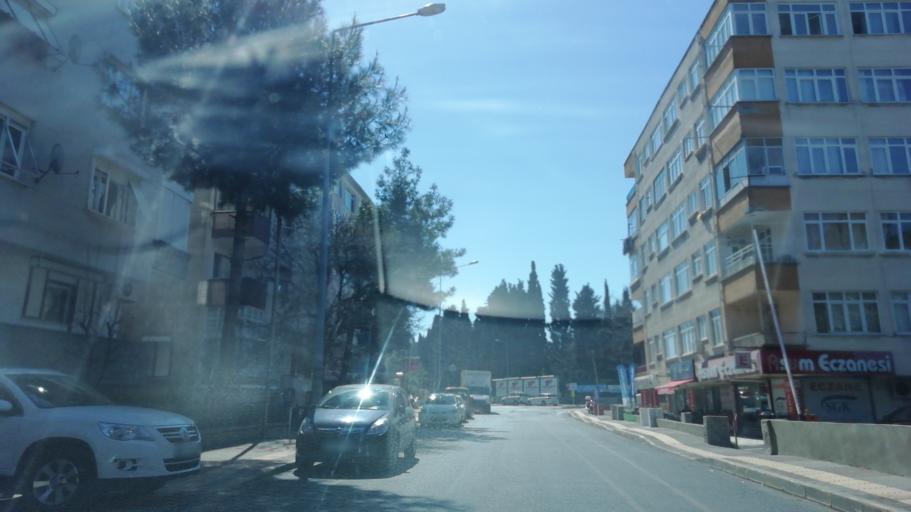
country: TR
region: Istanbul
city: Bahcelievler
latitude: 40.9880
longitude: 28.8660
